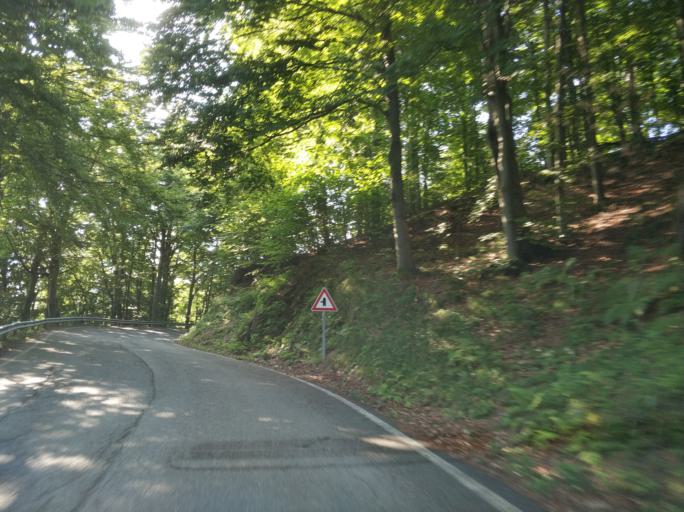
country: IT
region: Piedmont
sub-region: Provincia di Torino
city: Viu
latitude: 45.1987
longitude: 7.3706
